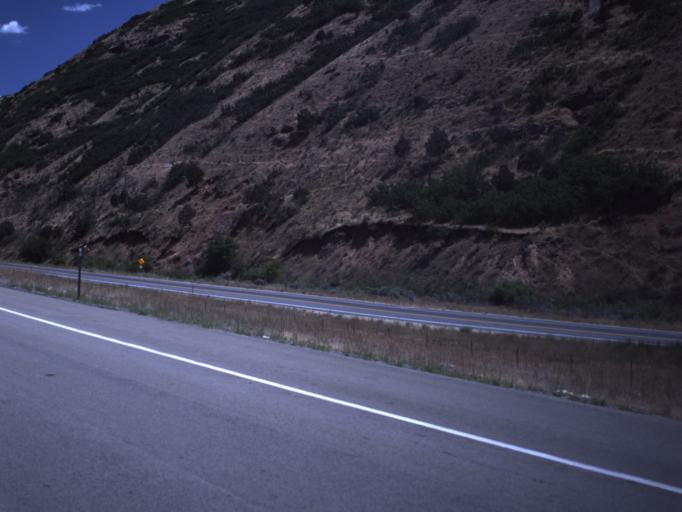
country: US
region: Utah
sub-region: Summit County
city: Coalville
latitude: 40.9734
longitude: -111.4343
